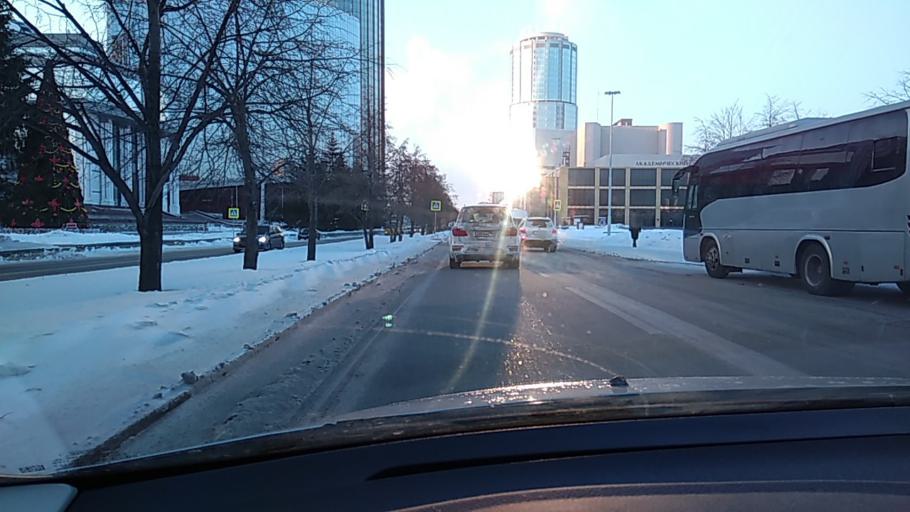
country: RU
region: Sverdlovsk
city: Yekaterinburg
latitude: 56.8421
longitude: 60.5957
